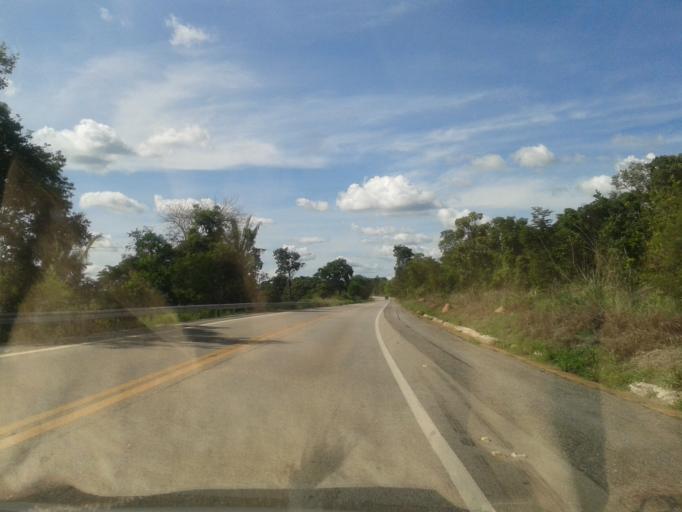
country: BR
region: Goias
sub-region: Mozarlandia
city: Mozarlandia
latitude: -15.1766
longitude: -50.5617
